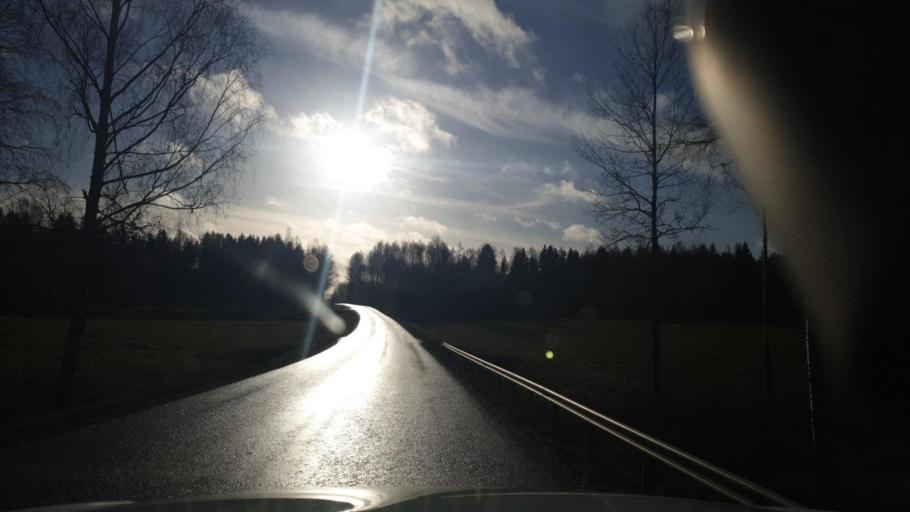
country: SE
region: Vaermland
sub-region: Eda Kommun
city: Charlottenberg
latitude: 59.7925
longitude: 12.1542
